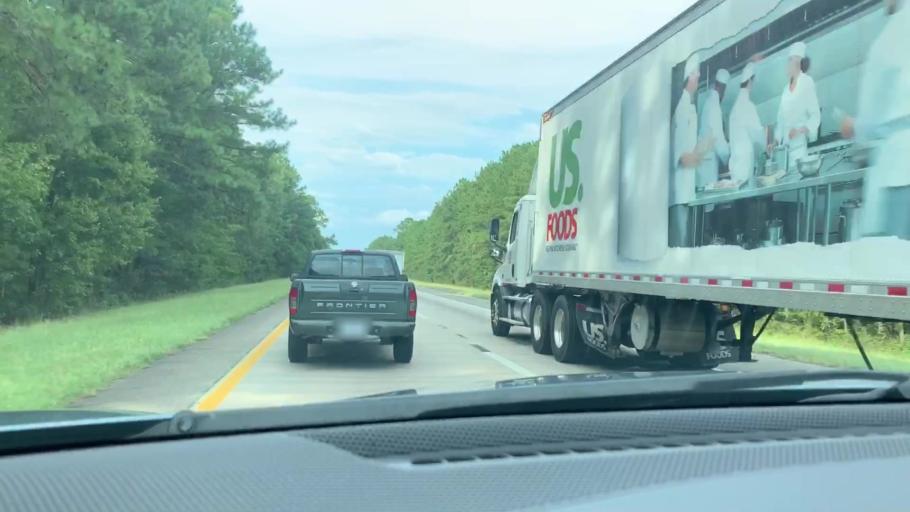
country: US
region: South Carolina
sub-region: Colleton County
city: Walterboro
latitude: 32.9878
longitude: -80.6722
